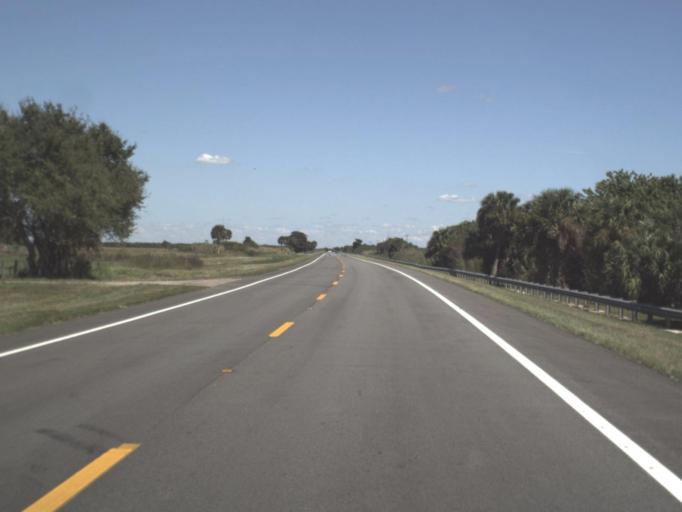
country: US
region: Florida
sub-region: Glades County
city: Buckhead Ridge
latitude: 27.0414
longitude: -80.9935
